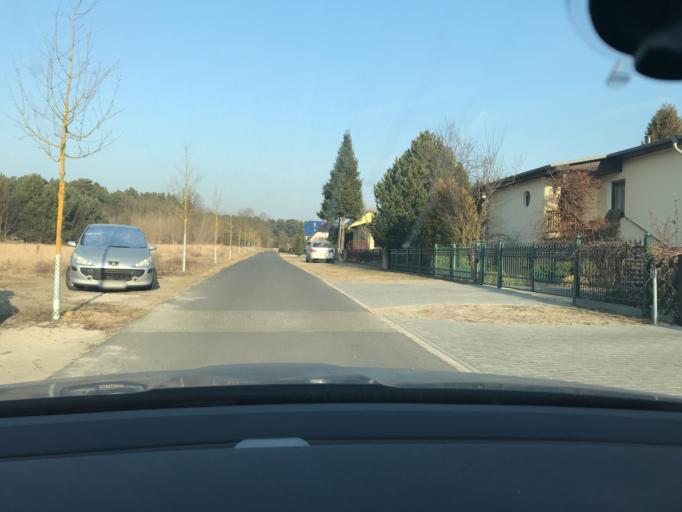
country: DE
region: Brandenburg
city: Munchehofe
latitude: 52.2204
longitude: 13.7753
